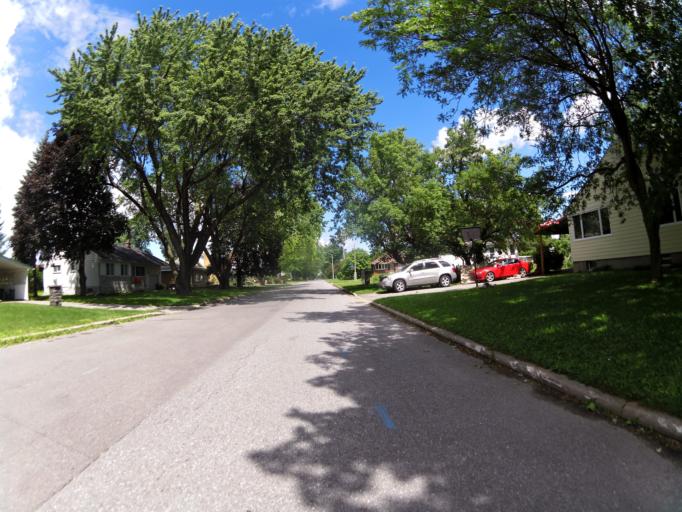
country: CA
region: Ontario
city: Ottawa
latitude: 45.3672
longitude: -75.7242
